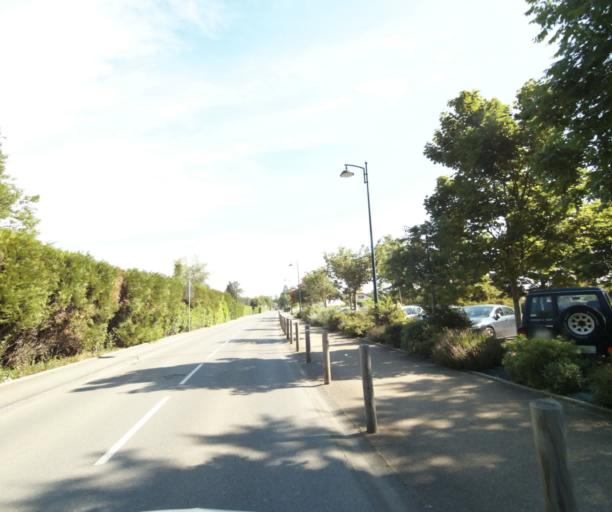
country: FR
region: Rhone-Alpes
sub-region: Departement de la Haute-Savoie
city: Marin
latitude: 46.3950
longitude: 6.5030
